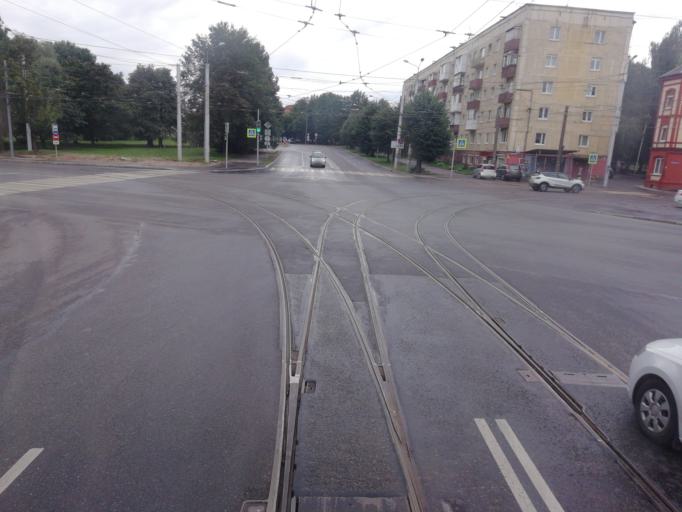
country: RU
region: Kaliningrad
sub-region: Gorod Kaliningrad
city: Kaliningrad
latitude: 54.6984
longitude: 20.5174
